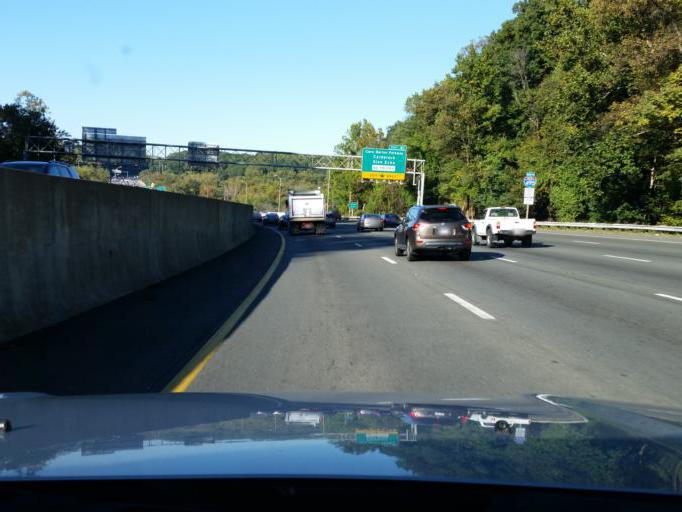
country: US
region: Maryland
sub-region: Montgomery County
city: Cabin John
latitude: 38.9660
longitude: -77.1804
